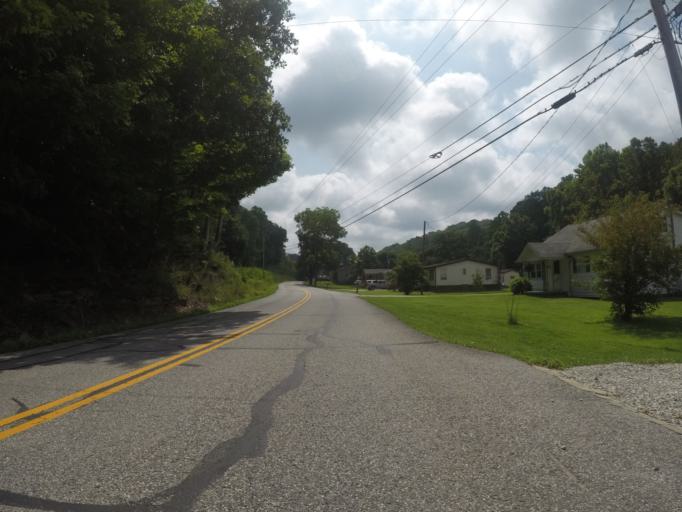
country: US
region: Kentucky
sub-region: Boyd County
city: Meads
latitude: 38.4131
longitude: -82.6799
